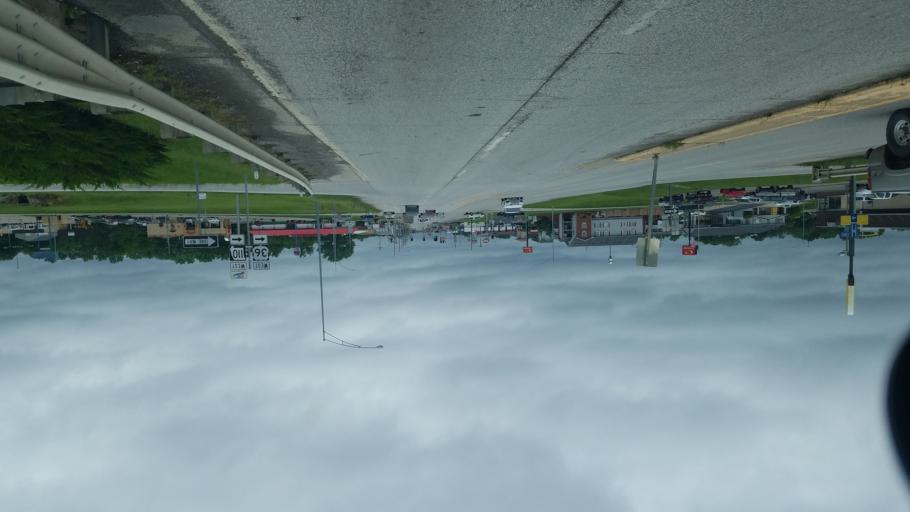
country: US
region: Missouri
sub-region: Livingston County
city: Chillicothe
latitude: 39.7733
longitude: -93.5526
